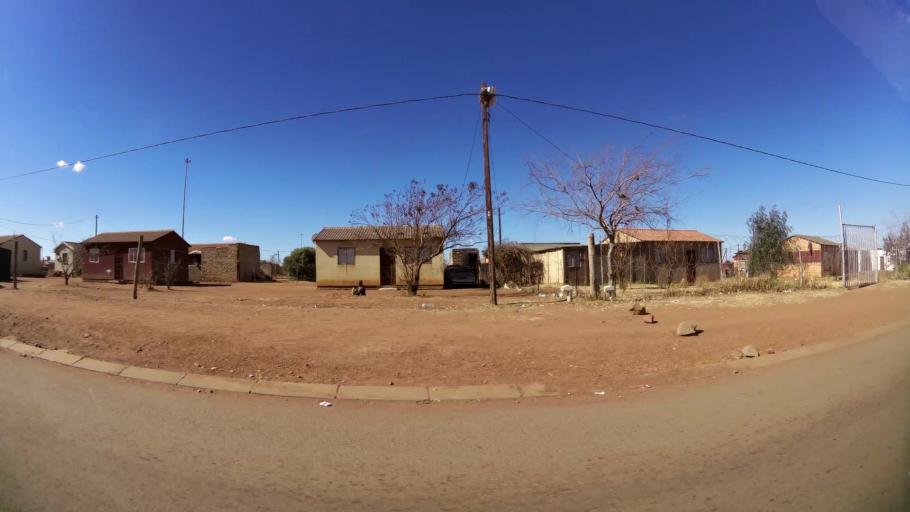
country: ZA
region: North-West
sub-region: Dr Kenneth Kaunda District Municipality
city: Klerksdorp
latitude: -26.8749
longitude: 26.5643
